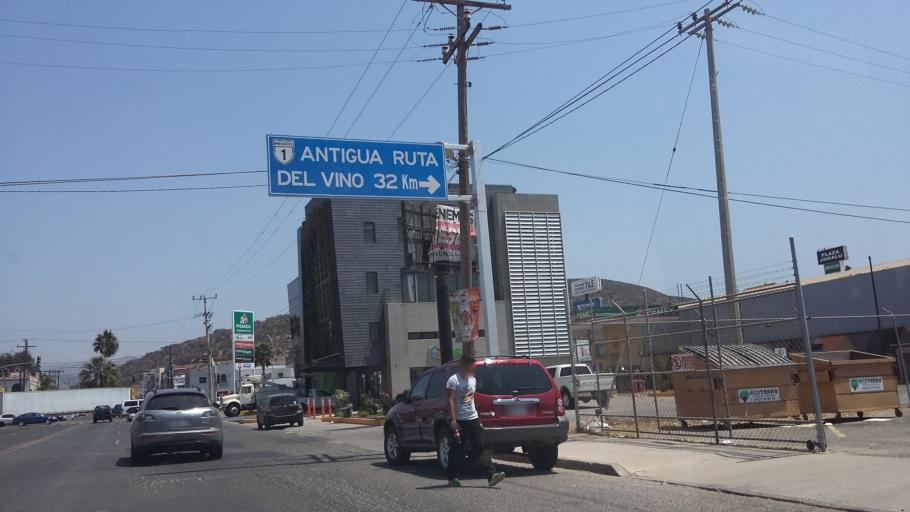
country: MX
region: Baja California
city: Ensenada
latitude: 31.8416
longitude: -116.6042
